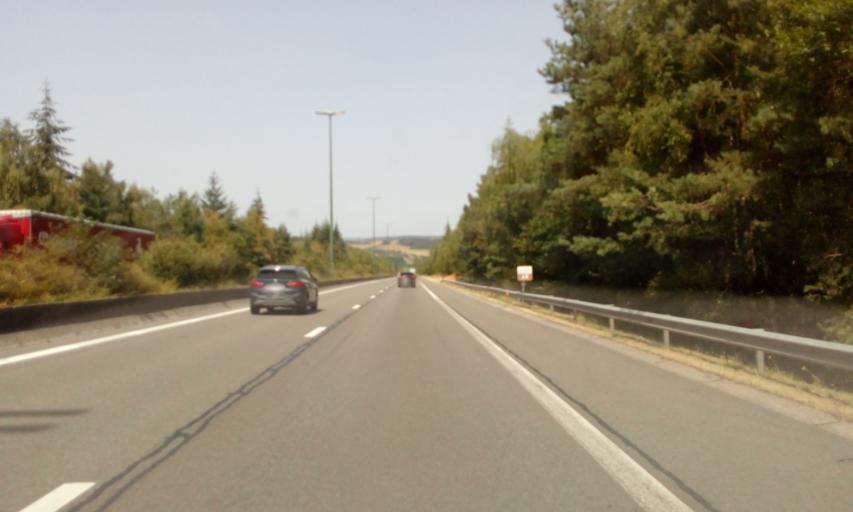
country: BE
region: Wallonia
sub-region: Province du Luxembourg
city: Tellin
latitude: 50.0717
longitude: 5.1832
